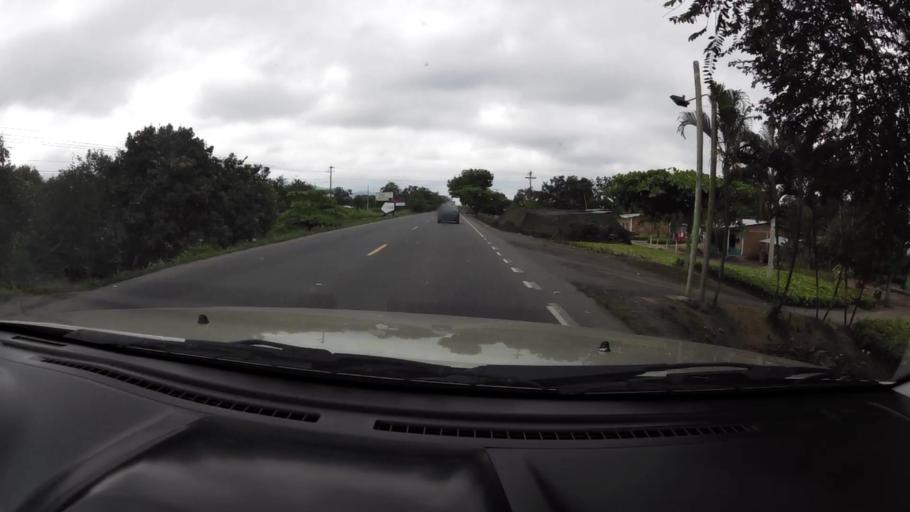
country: EC
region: Guayas
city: Naranjal
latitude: -2.7257
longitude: -79.6738
